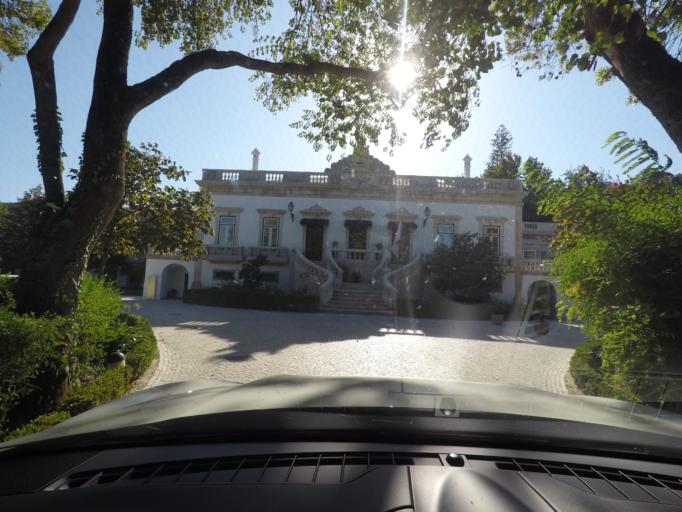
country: PT
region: Coimbra
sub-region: Coimbra
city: Coimbra
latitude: 40.1983
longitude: -8.4331
